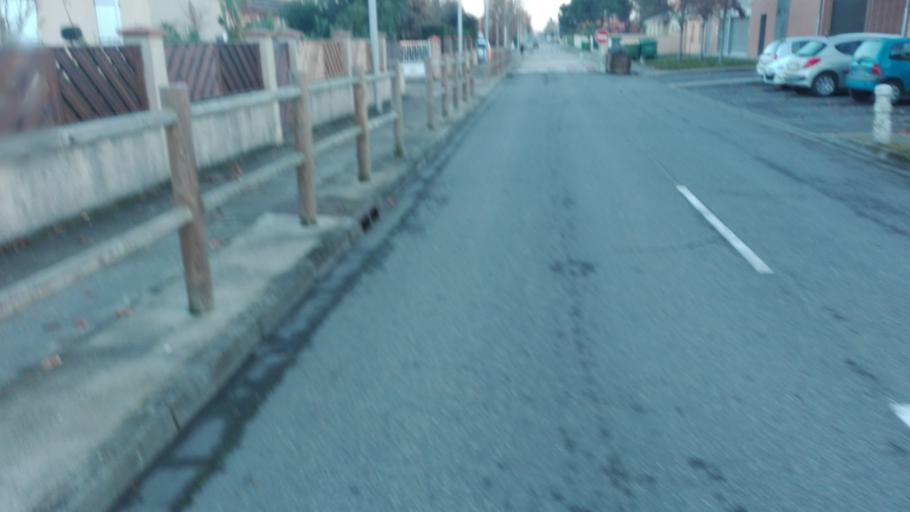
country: FR
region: Midi-Pyrenees
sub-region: Departement de la Haute-Garonne
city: Grenade
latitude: 43.7678
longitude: 1.2976
